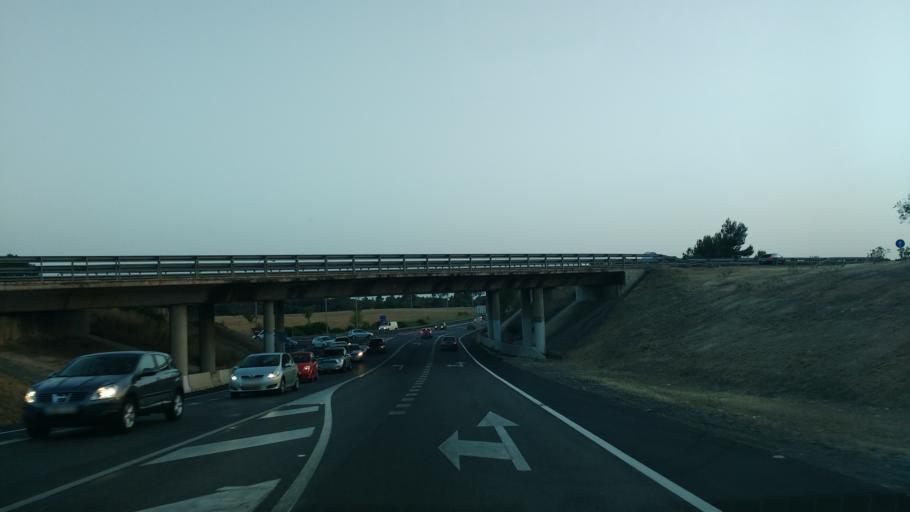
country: ES
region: Balearic Islands
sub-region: Illes Balears
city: Marratxi
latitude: 39.6305
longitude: 2.7367
